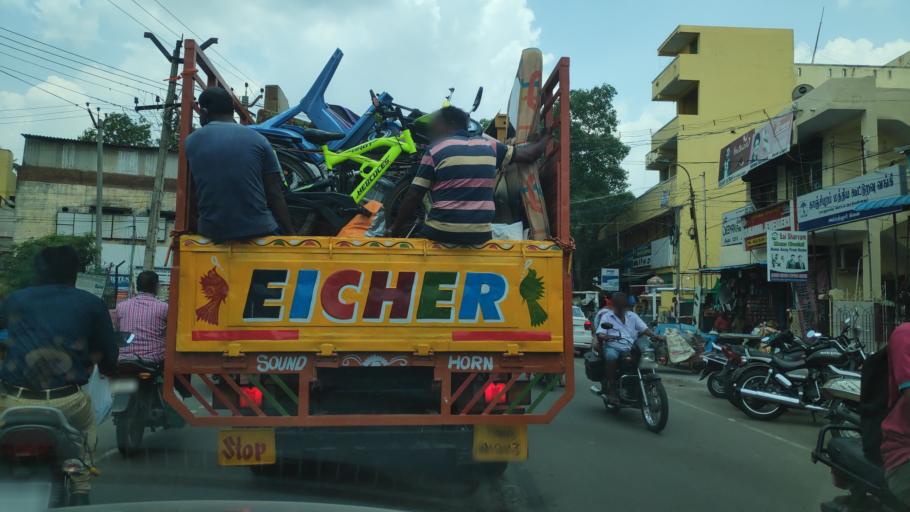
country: IN
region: Tamil Nadu
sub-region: Thiruvallur
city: Ambattur
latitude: 13.1184
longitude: 80.1523
